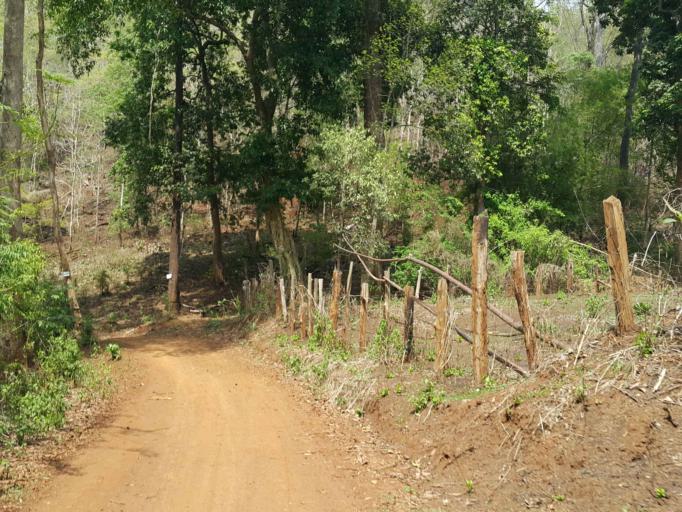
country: TH
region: Chiang Mai
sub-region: Amphoe Chiang Dao
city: Chiang Dao
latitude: 19.3106
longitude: 98.7243
